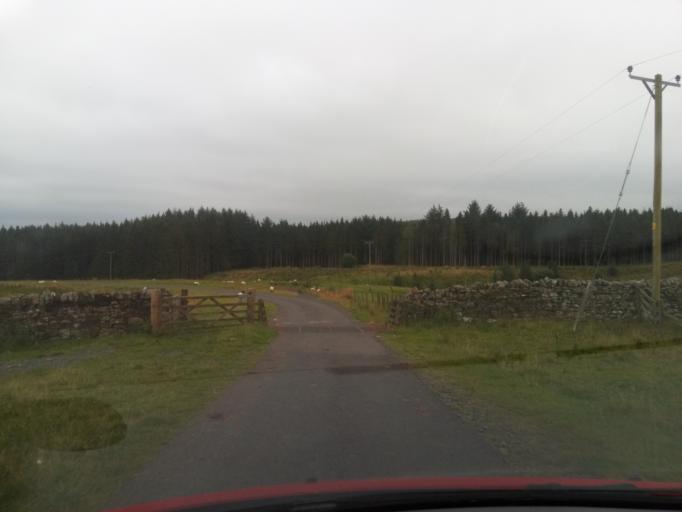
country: GB
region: England
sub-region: Northumberland
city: Rochester
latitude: 55.2909
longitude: -2.2161
